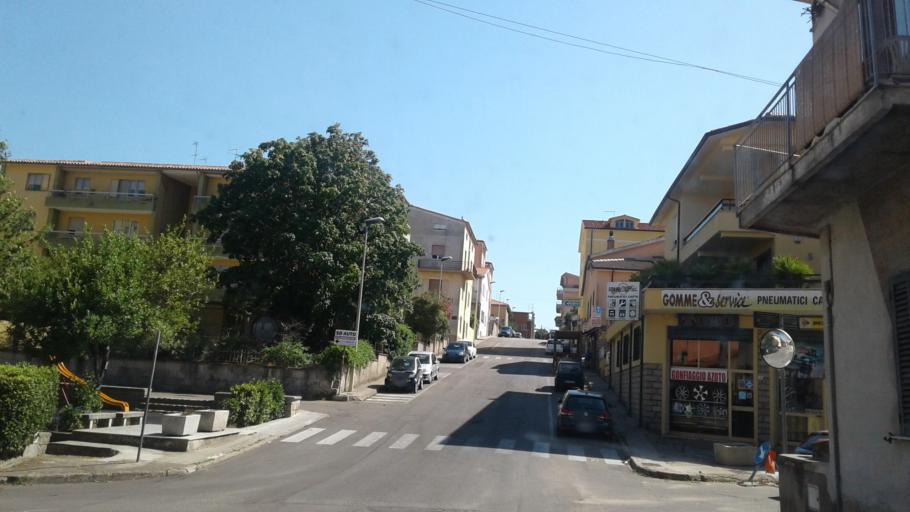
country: IT
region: Sardinia
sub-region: Provincia di Olbia-Tempio
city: Tempio Pausania
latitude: 40.8988
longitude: 9.1082
